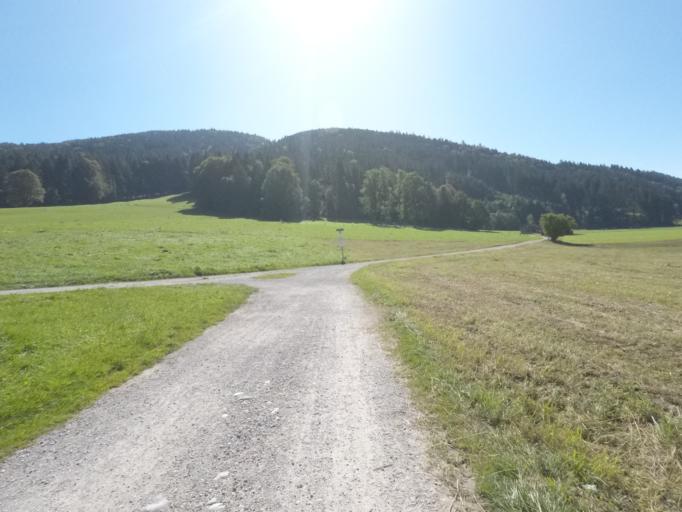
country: DE
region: Bavaria
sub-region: Upper Bavaria
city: Gaissach
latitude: 47.7411
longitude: 11.5998
